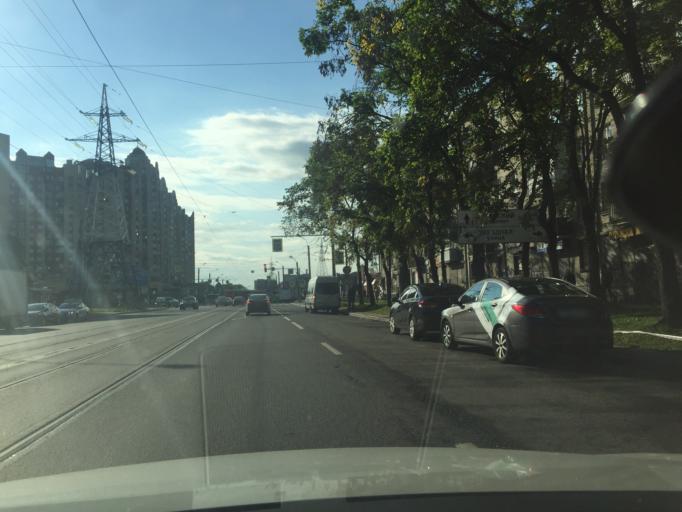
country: RU
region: St.-Petersburg
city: Kupchino
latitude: 59.8342
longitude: 30.3464
